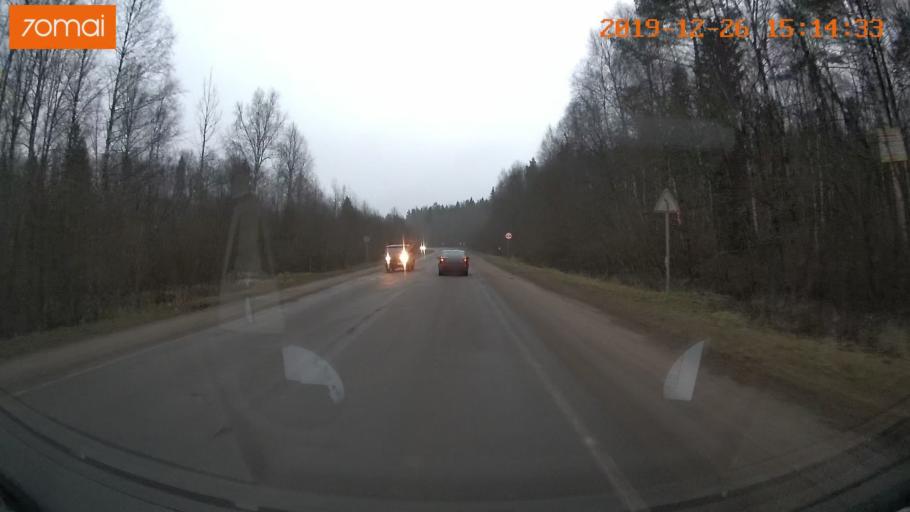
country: RU
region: Jaroslavl
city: Rybinsk
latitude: 58.1050
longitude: 38.8791
